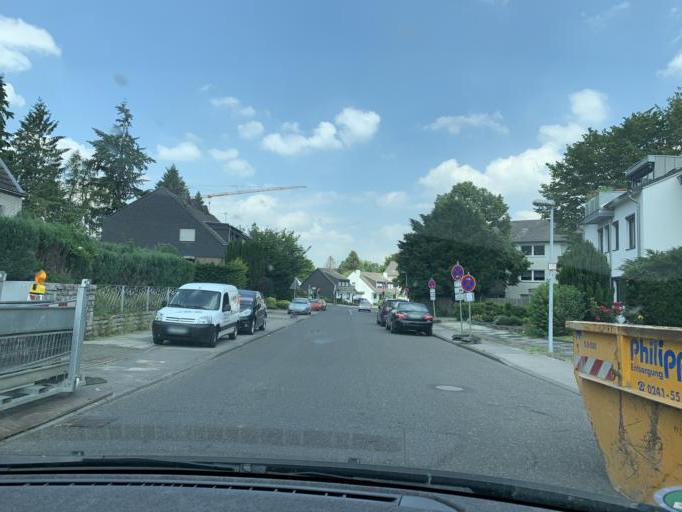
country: DE
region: North Rhine-Westphalia
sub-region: Regierungsbezirk Koln
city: Aachen
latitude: 50.7893
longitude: 6.0890
